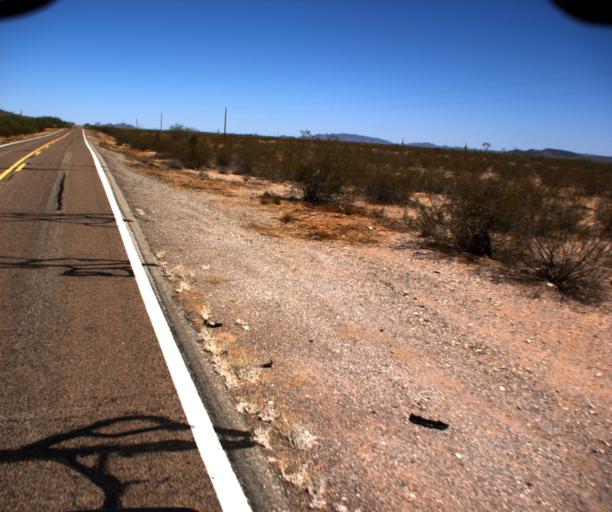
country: US
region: Arizona
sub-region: Pima County
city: Ajo
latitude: 32.2028
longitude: -112.5165
